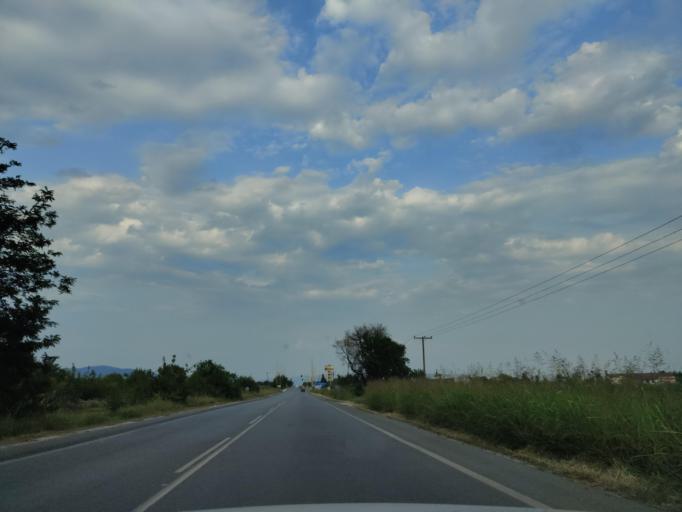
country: GR
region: East Macedonia and Thrace
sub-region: Nomos Dramas
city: Xiropotamos
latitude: 41.1643
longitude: 24.0670
